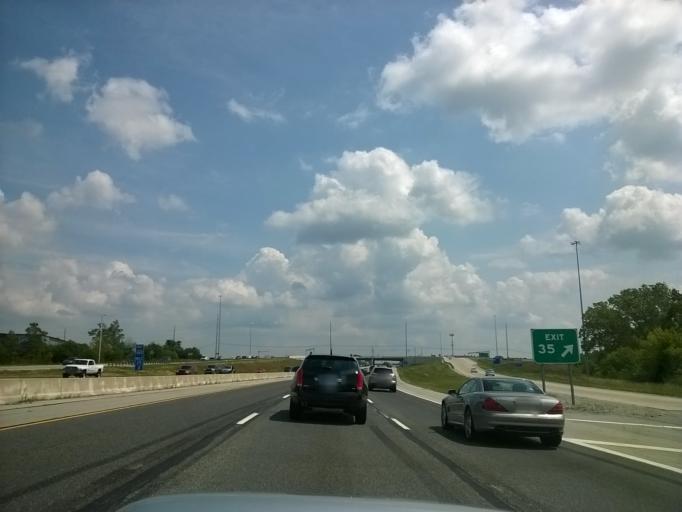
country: US
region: Indiana
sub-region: Marion County
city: Broad Ripple
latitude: 39.9121
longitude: -86.0814
